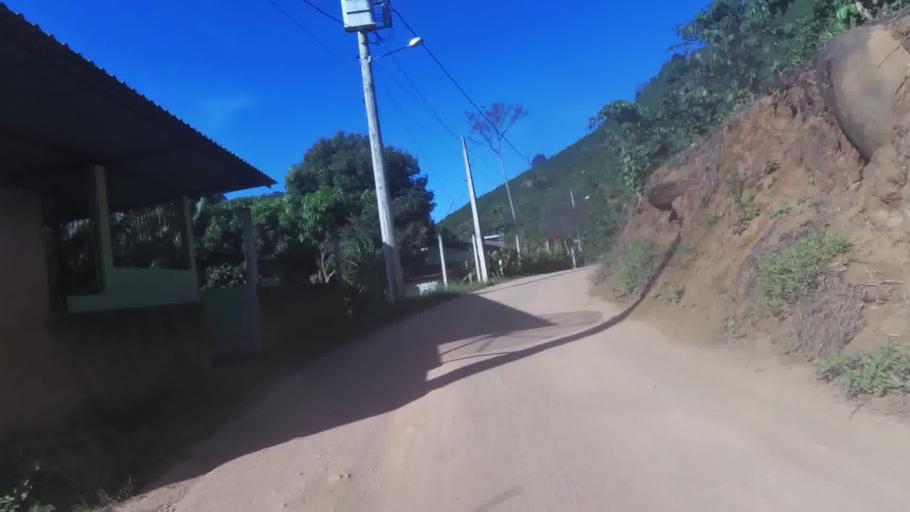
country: BR
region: Espirito Santo
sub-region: Iconha
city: Iconha
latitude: -20.7629
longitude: -40.8290
